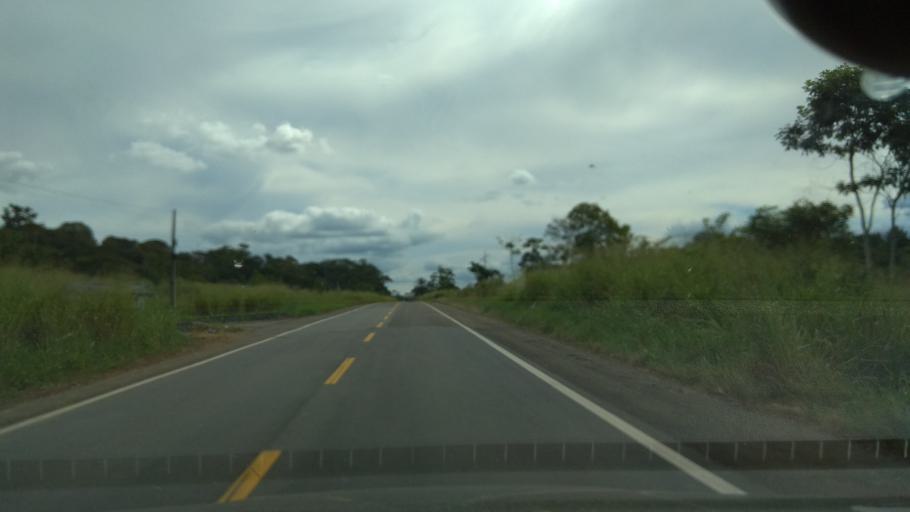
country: BR
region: Bahia
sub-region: Ipiau
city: Ipiau
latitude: -14.1945
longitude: -39.6423
